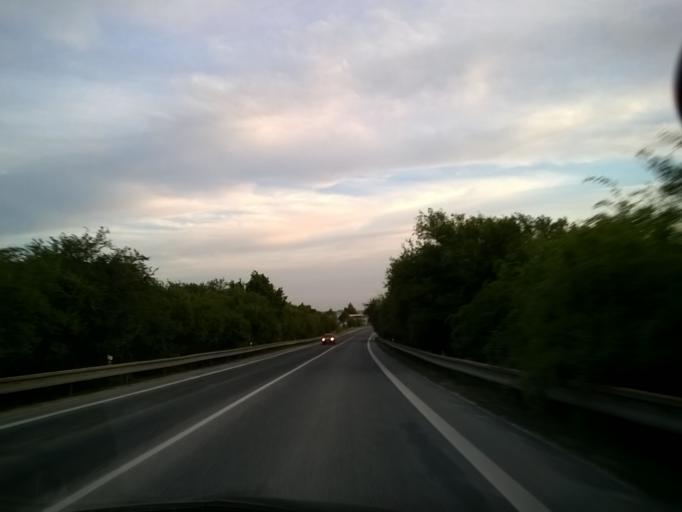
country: SK
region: Nitriansky
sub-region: Okres Nitra
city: Nitra
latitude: 48.3533
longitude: 18.1800
